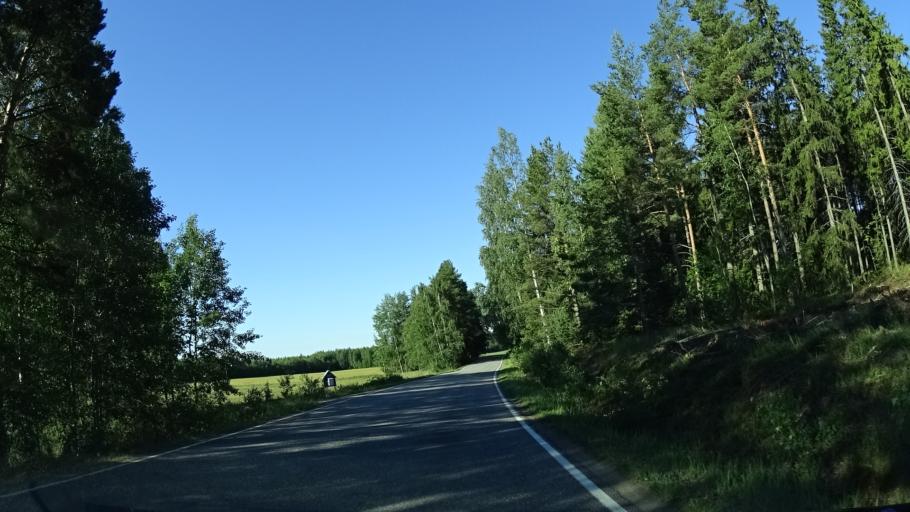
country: FI
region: Varsinais-Suomi
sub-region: Turku
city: Merimasku
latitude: 60.5027
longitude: 21.8106
